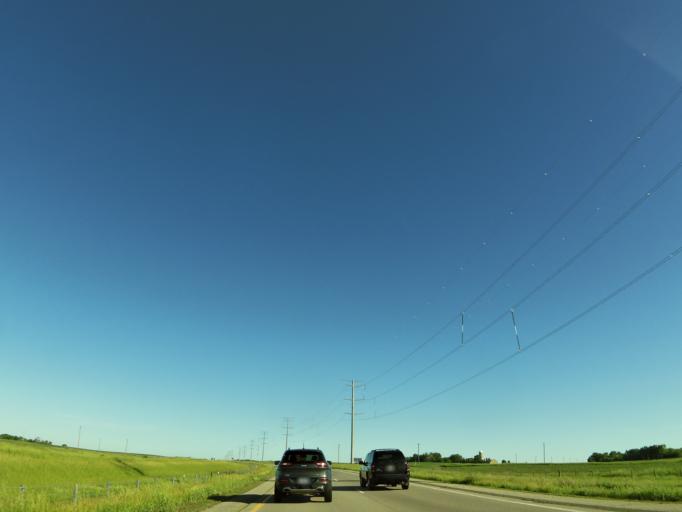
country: US
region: Minnesota
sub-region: Douglas County
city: Osakis
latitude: 45.8078
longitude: -95.1086
